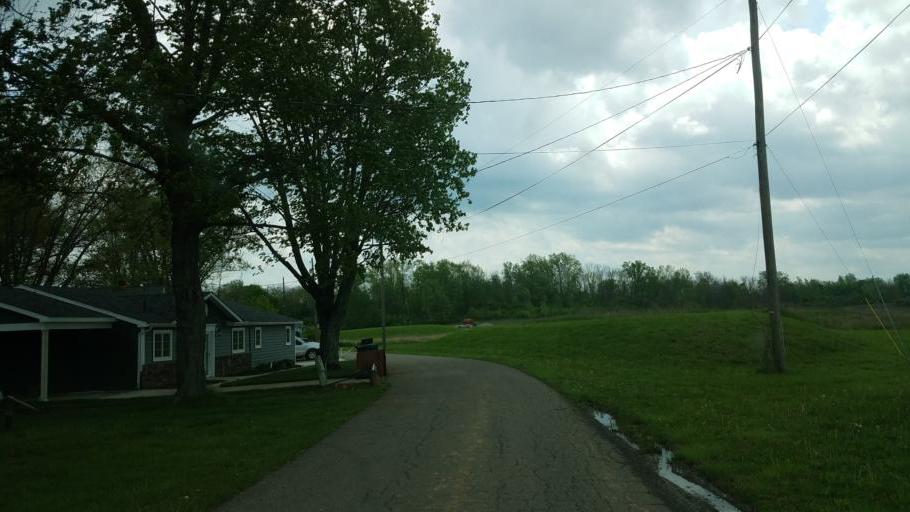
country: US
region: Ohio
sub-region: Licking County
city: Harbor Hills
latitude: 39.9250
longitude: -82.4378
